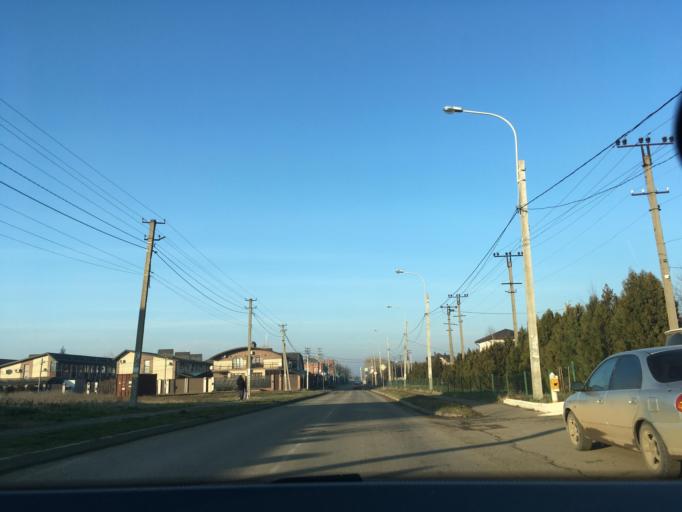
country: RU
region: Krasnodarskiy
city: Krasnodar
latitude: 45.1179
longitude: 39.0145
